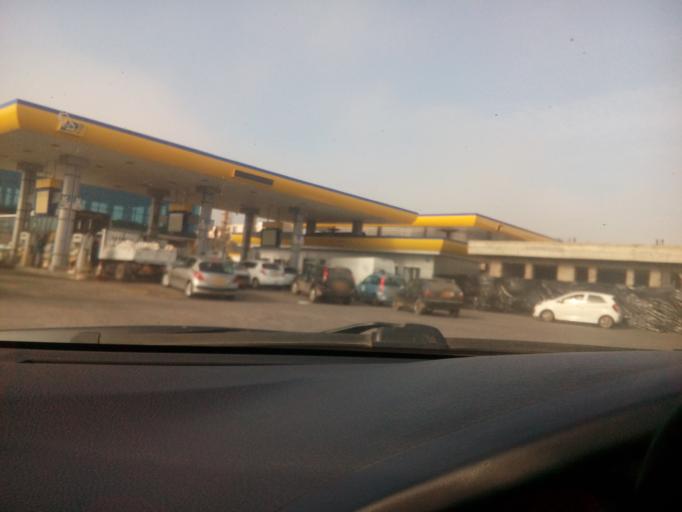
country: DZ
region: Oran
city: Es Senia
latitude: 35.6556
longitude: -0.6235
